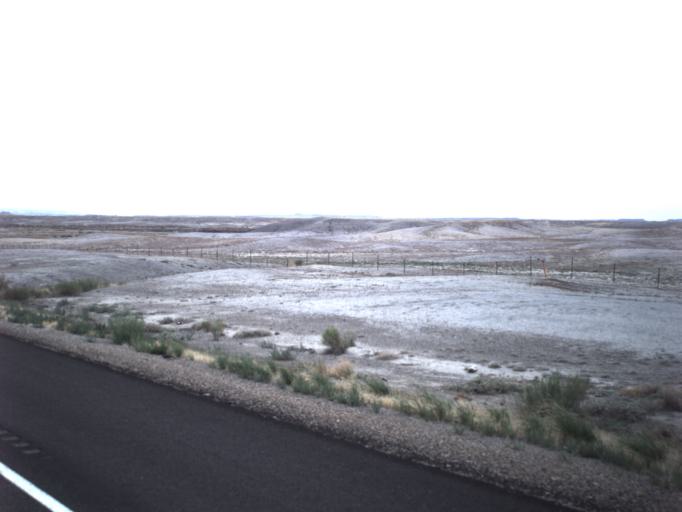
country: US
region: Utah
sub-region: Carbon County
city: East Carbon City
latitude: 38.9864
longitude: -110.2410
